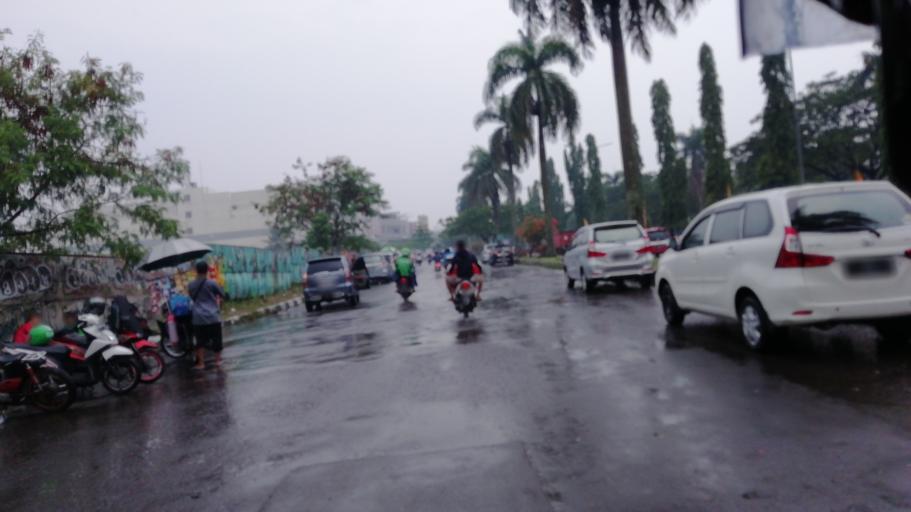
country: ID
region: West Java
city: Cibinong
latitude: -6.4849
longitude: 106.8396
